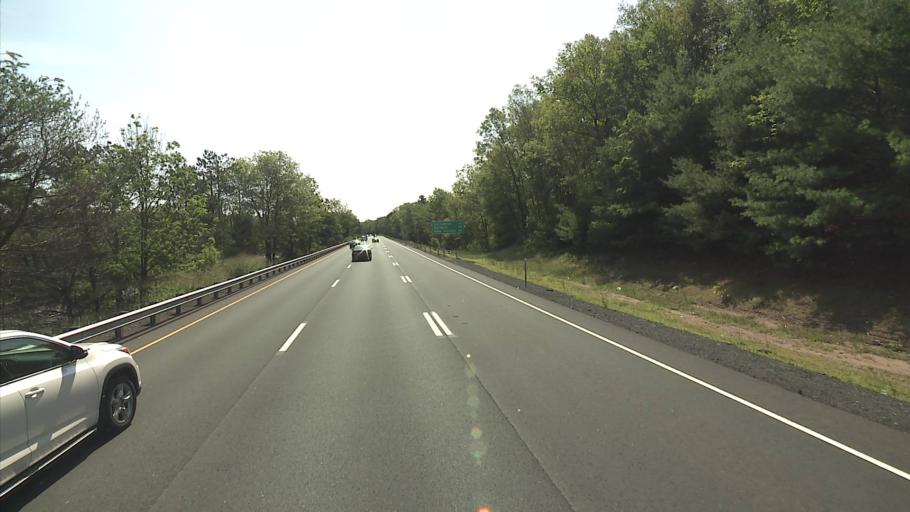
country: US
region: Connecticut
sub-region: Hartford County
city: Terramuggus
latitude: 41.6609
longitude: -72.5204
